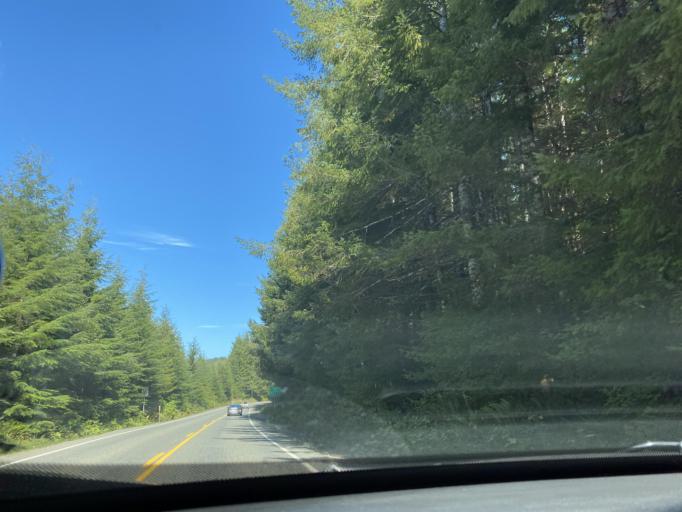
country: US
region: Washington
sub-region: Clallam County
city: Forks
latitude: 47.9493
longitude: -124.4622
